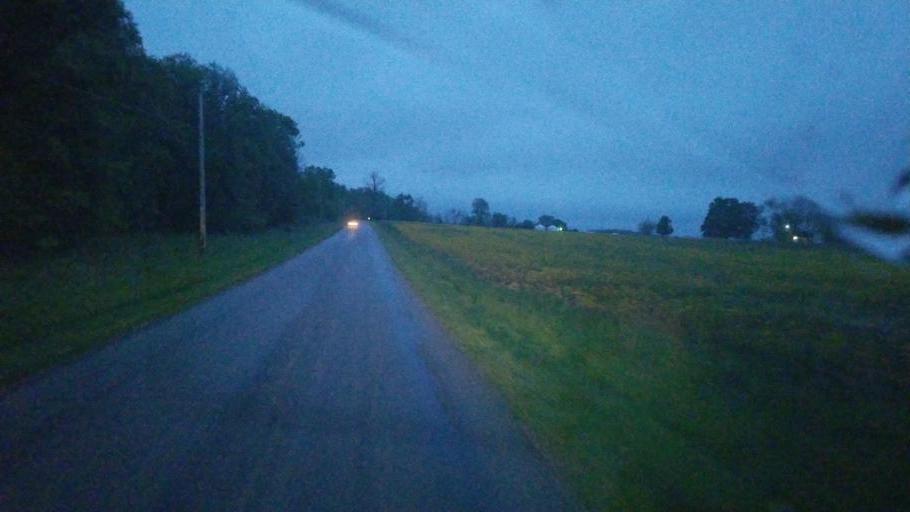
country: US
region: Ohio
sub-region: Highland County
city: Greenfield
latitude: 39.3417
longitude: -83.4387
